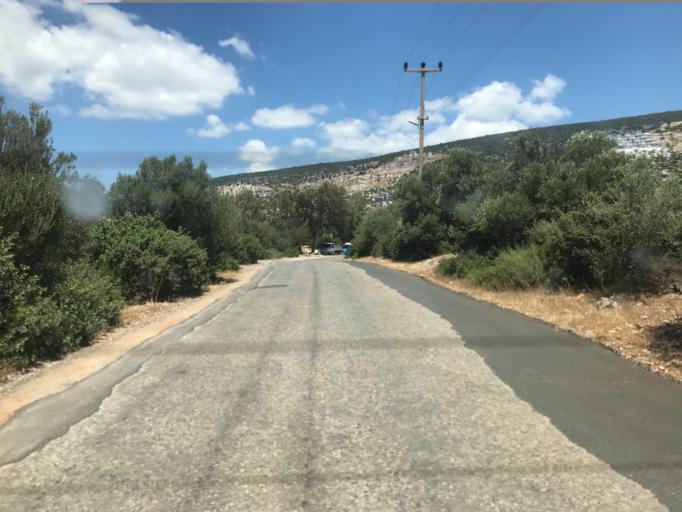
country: TR
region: Aydin
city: Sarikemer
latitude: 37.4118
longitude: 27.4227
